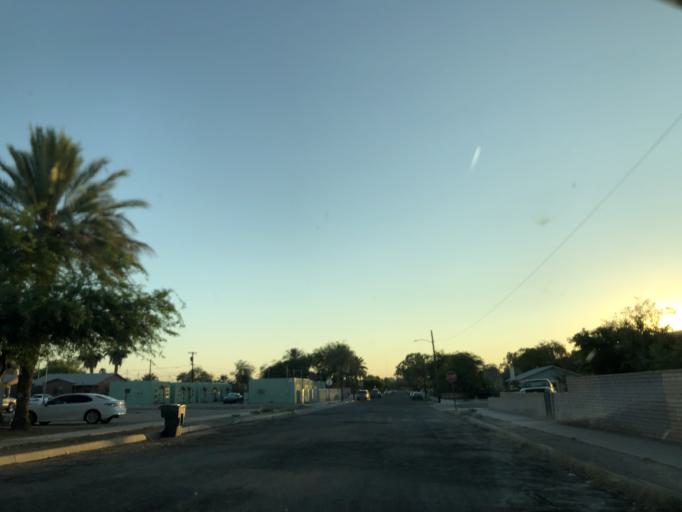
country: US
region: Arizona
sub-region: Yuma County
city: Yuma
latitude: 32.7234
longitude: -114.6277
